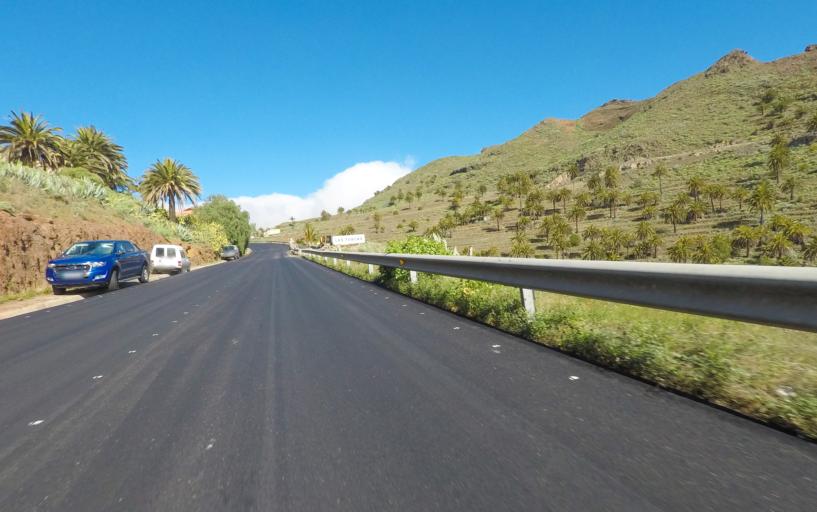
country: ES
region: Canary Islands
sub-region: Provincia de Santa Cruz de Tenerife
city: Alajero
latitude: 28.0744
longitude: -17.2075
